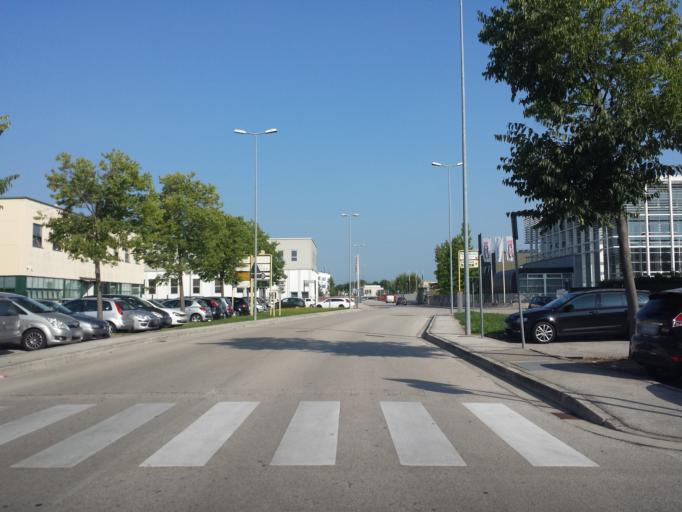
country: IT
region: Veneto
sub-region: Provincia di Vicenza
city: Villaggio Montegrappa
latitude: 45.5254
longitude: 11.5895
